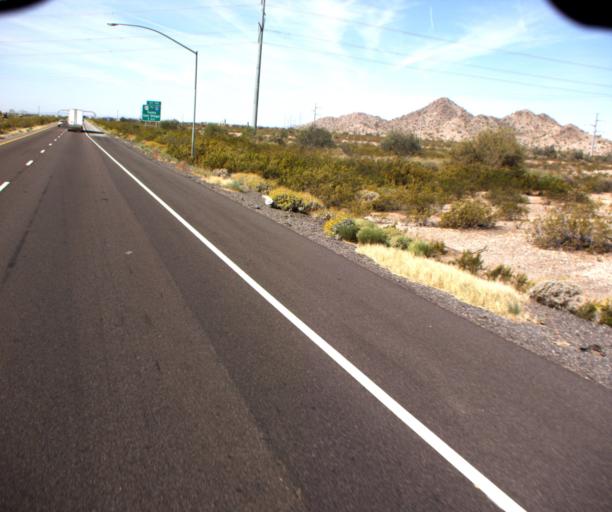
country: US
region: Arizona
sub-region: Maricopa County
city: Buckeye
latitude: 33.4314
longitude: -112.5981
